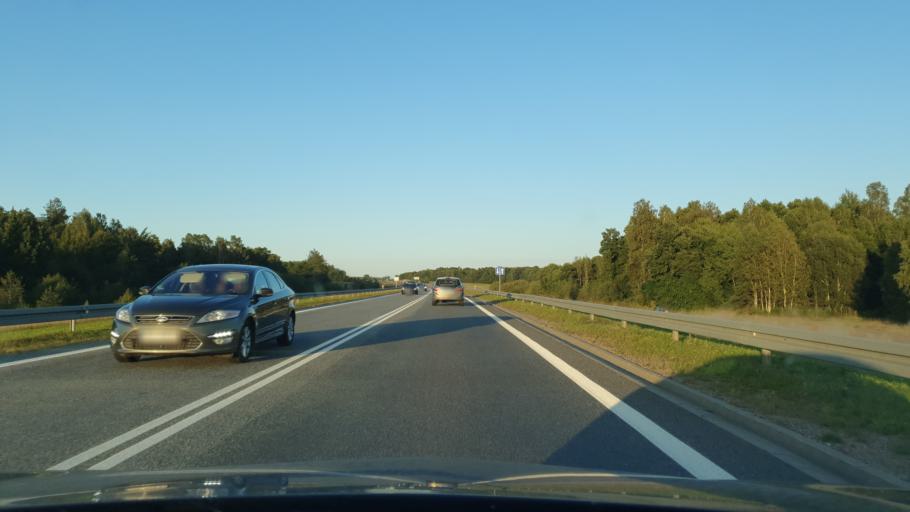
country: PL
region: Pomeranian Voivodeship
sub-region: Slupsk
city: Slupsk
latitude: 54.4582
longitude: 17.0988
